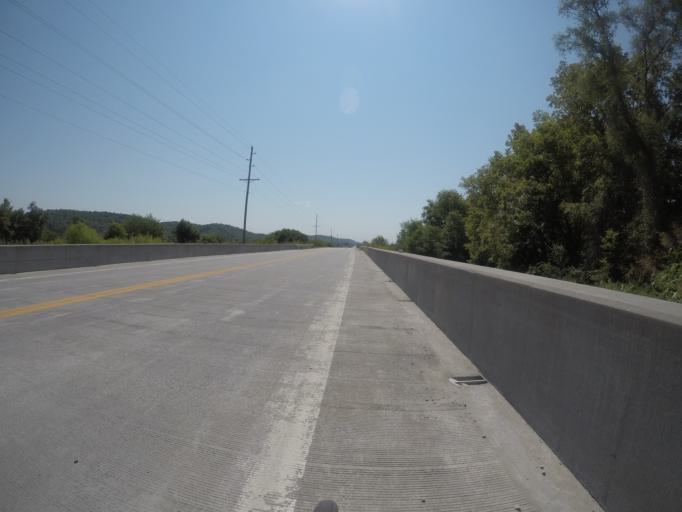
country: US
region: Kansas
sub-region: Atchison County
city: Atchison
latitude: 39.5215
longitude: -95.0266
